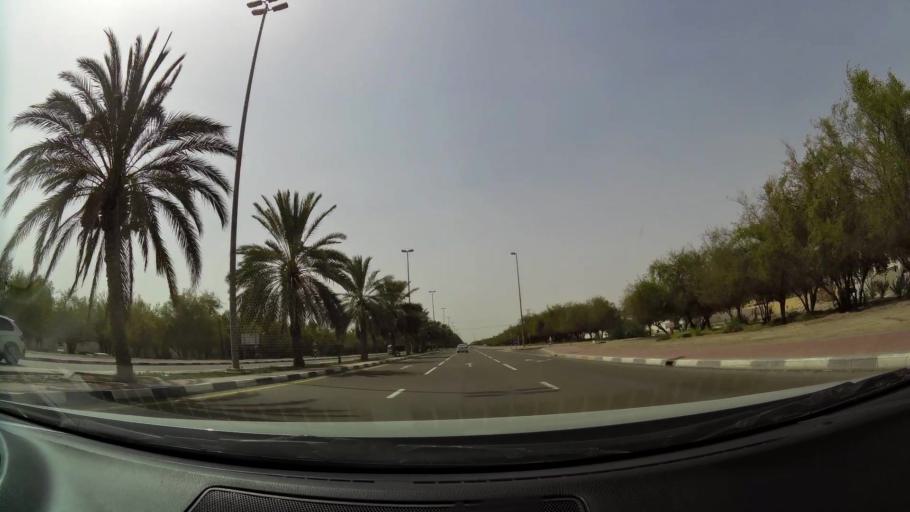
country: AE
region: Abu Dhabi
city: Al Ain
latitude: 24.1684
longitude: 55.6676
